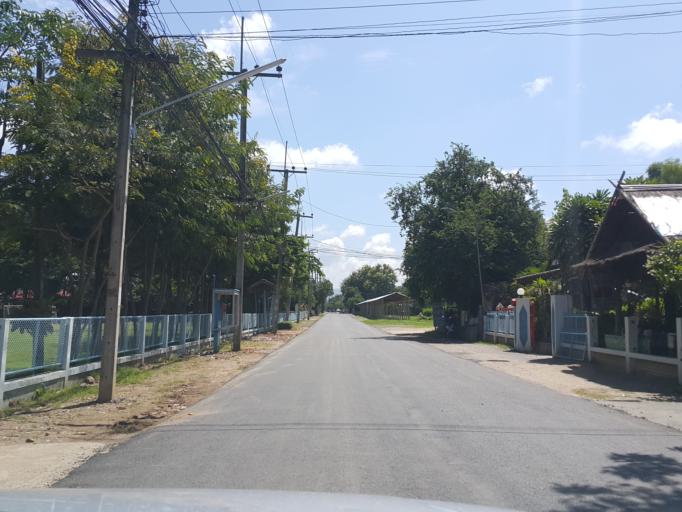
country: TH
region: Chiang Mai
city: San Kamphaeng
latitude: 18.7205
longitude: 99.1063
